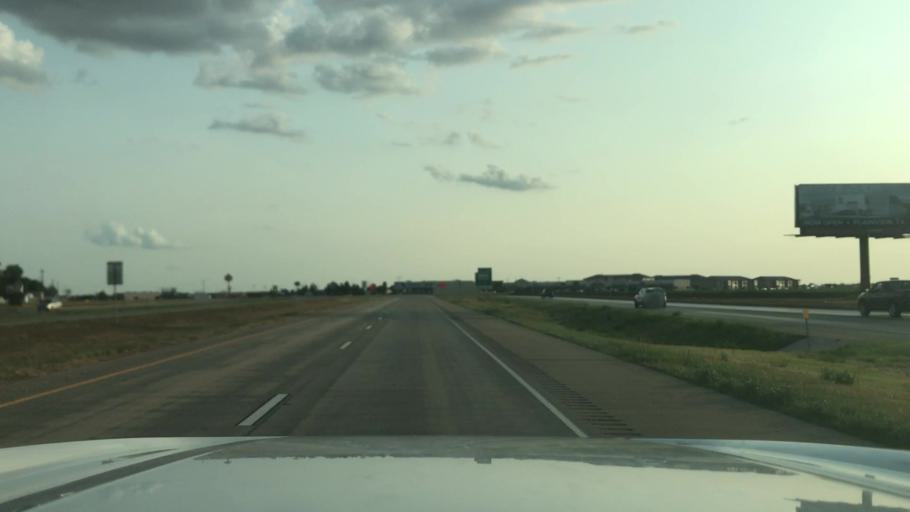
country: US
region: Texas
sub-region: Hale County
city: Plainview
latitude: 34.2009
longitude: -101.7462
